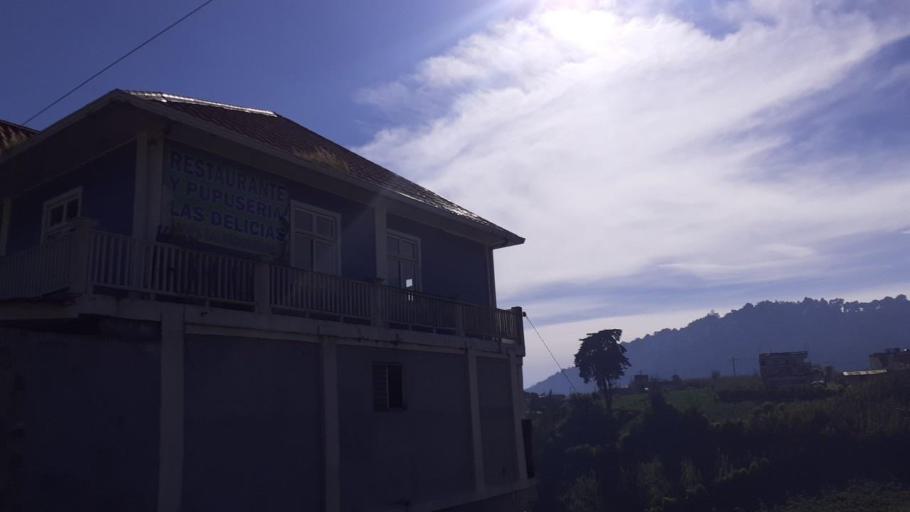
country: GT
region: Quetzaltenango
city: Ostuncalco
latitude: 14.8634
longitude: -91.6231
